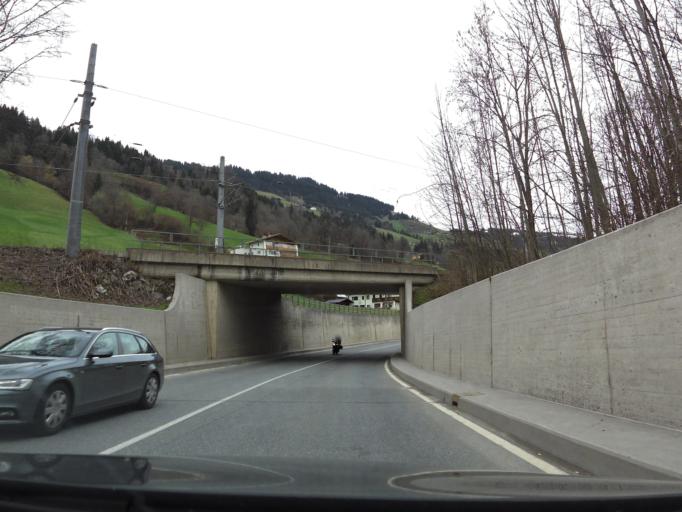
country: AT
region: Tyrol
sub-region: Politischer Bezirk Kitzbuhel
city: Westendorf
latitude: 47.4378
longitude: 12.2149
